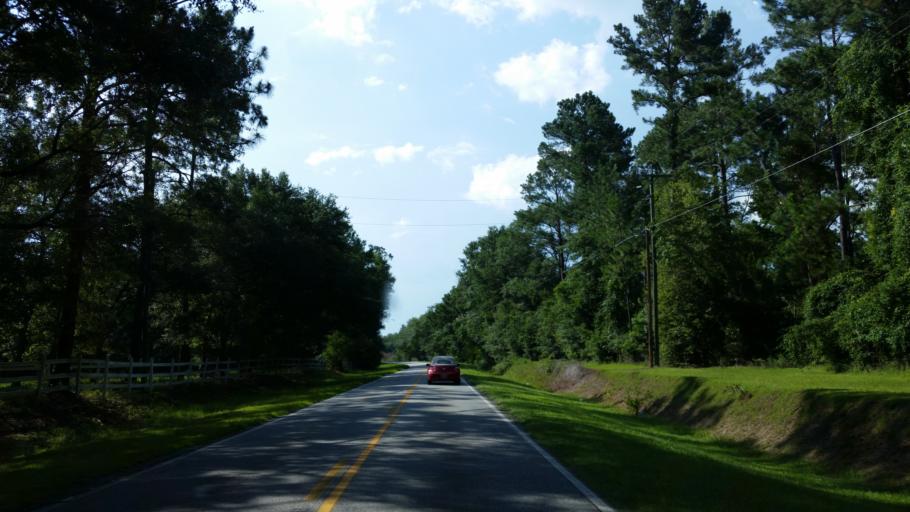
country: US
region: Georgia
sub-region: Lowndes County
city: Hahira
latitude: 30.9148
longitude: -83.3858
